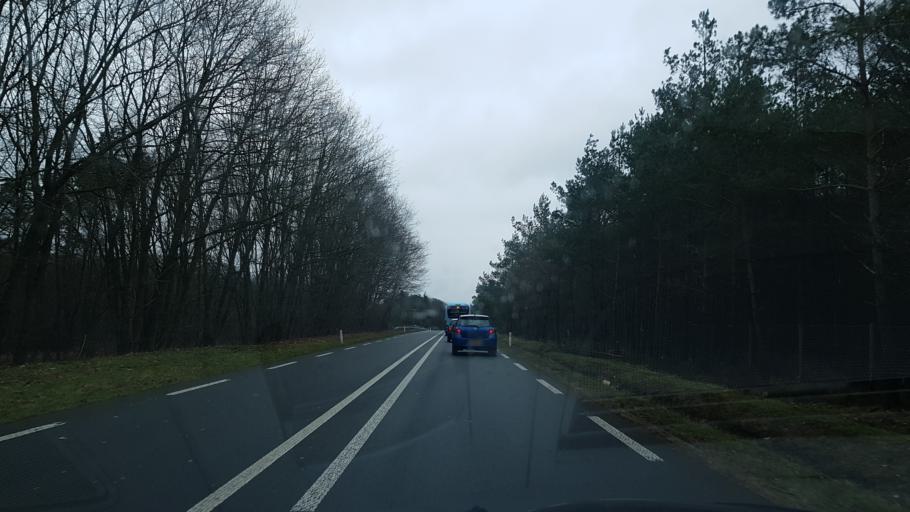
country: NL
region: Gelderland
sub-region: Gemeente Apeldoorn
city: Beekbergen
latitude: 52.1201
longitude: 5.9553
